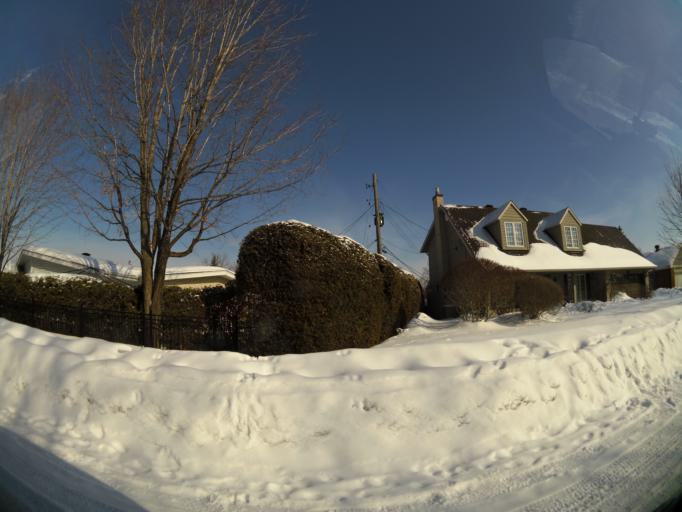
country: CA
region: Ontario
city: Ottawa
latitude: 45.3903
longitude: -75.6446
